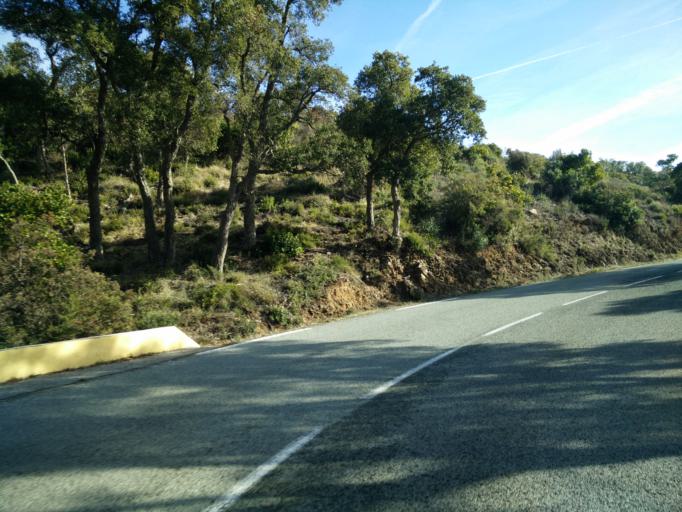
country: FR
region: Provence-Alpes-Cote d'Azur
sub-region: Departement du Var
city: Saint-Raphael
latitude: 43.5030
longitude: 6.7859
